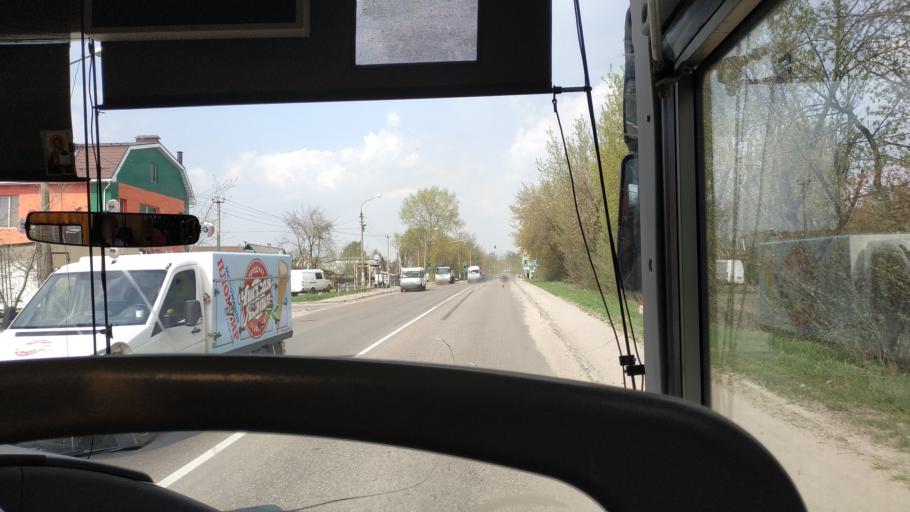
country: RU
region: Moskovskaya
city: Tomilino
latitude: 55.6269
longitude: 37.9262
